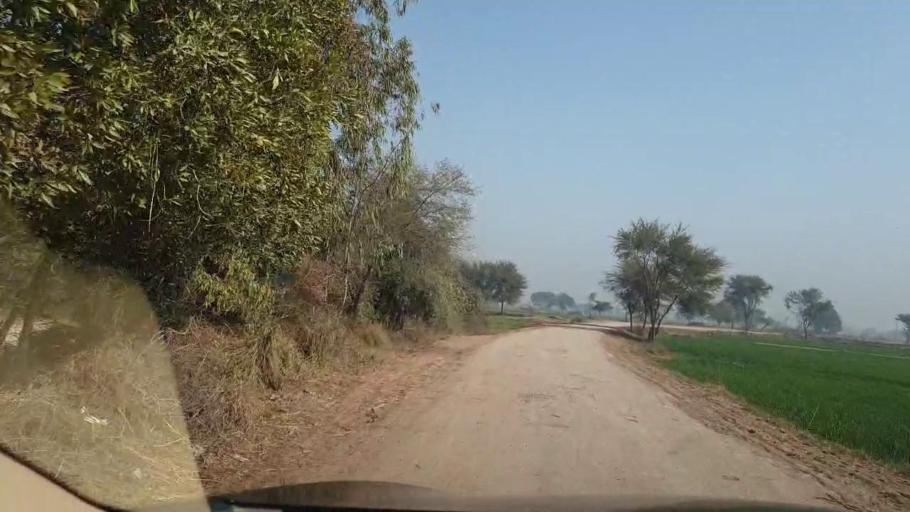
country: PK
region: Sindh
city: Ubauro
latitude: 28.1139
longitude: 69.7312
